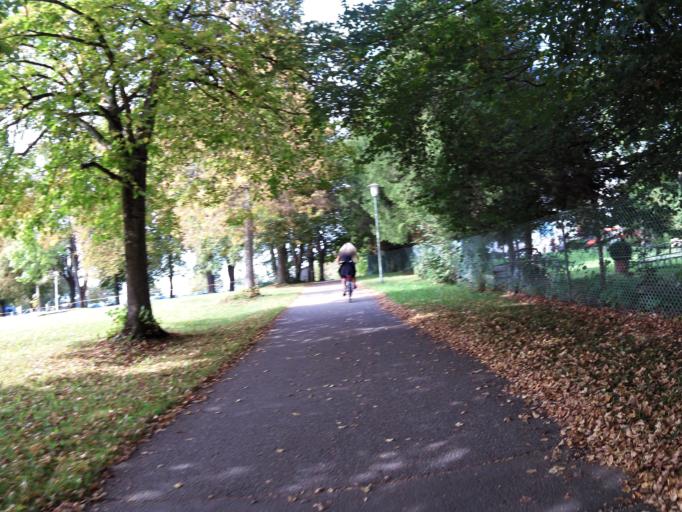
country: DE
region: Bavaria
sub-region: Upper Bavaria
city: Bernried
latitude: 47.8744
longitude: 11.2829
